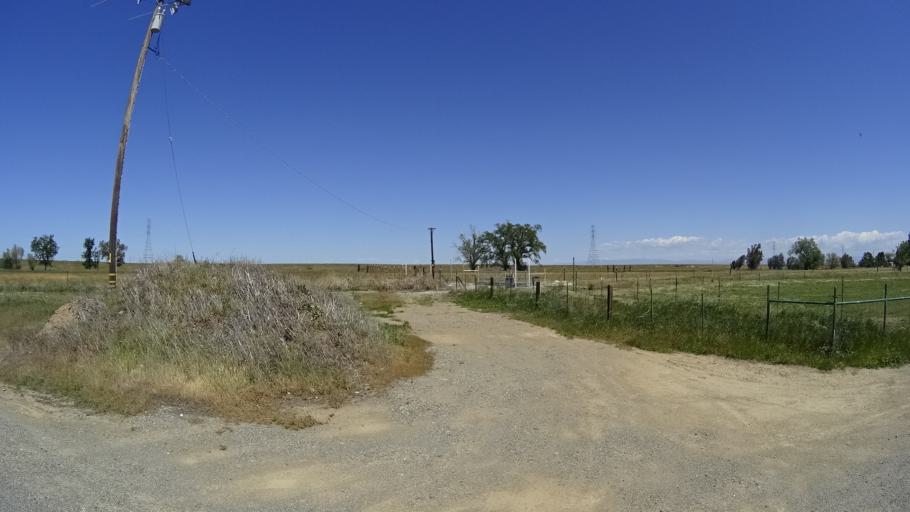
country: US
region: California
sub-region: Glenn County
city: Orland
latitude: 39.7980
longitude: -122.2568
